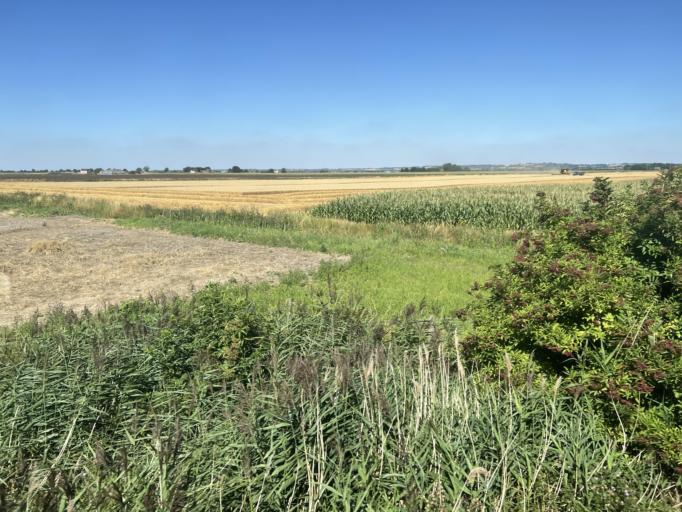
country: GB
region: England
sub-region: Lincolnshire
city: Spilsby
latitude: 53.0997
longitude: 0.1097
